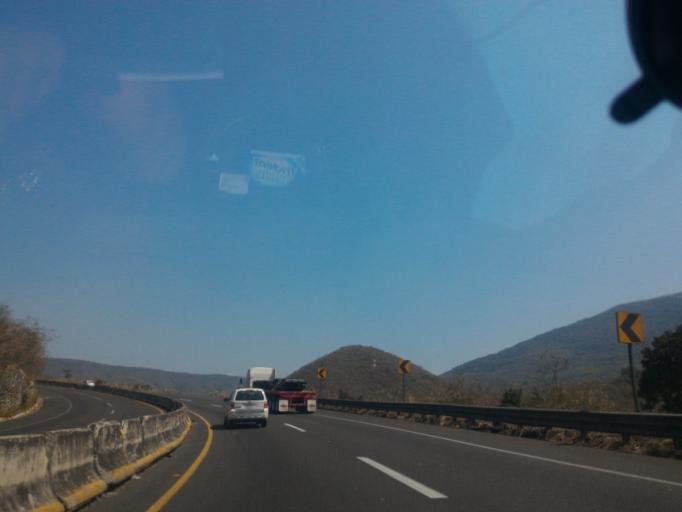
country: MX
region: Colima
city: Ixtlahuacan
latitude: 19.0221
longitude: -103.8077
